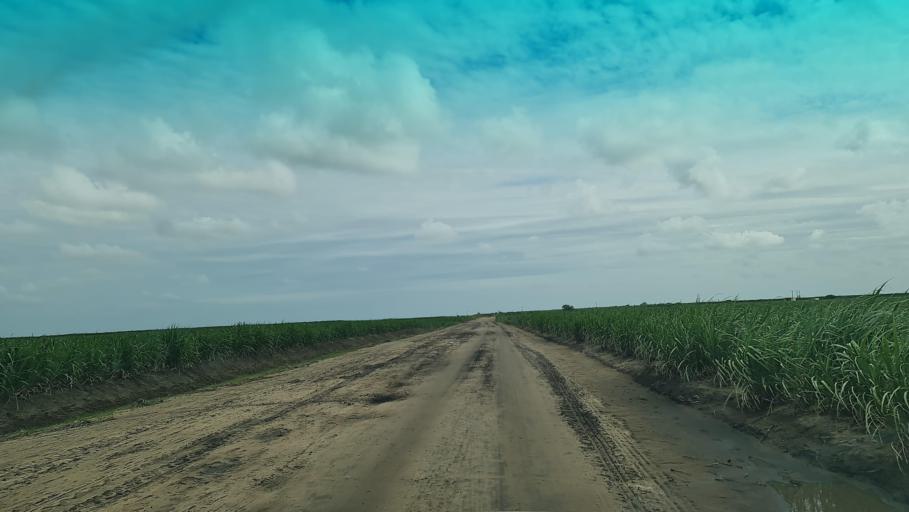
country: MZ
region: Maputo
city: Manhica
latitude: -25.4526
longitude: 32.8193
